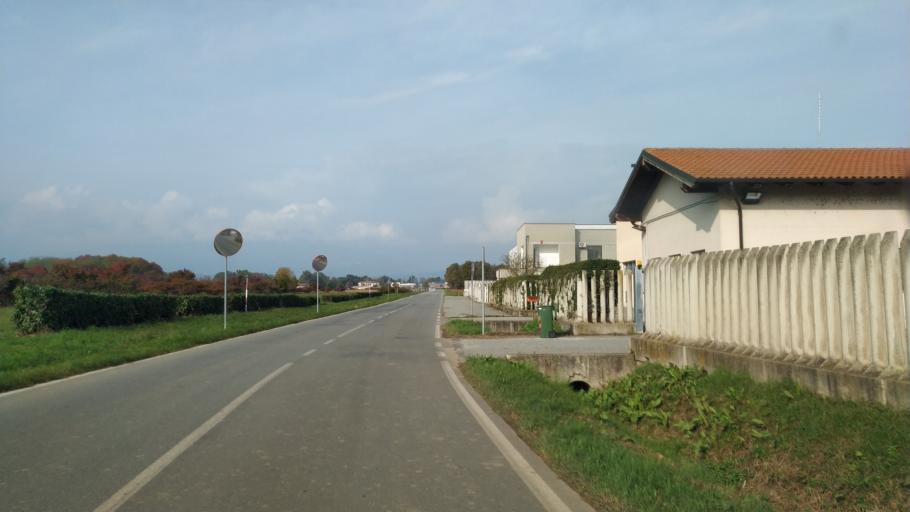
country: IT
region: Piedmont
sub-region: Provincia di Biella
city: Vergnasco
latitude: 45.4752
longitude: 8.0821
